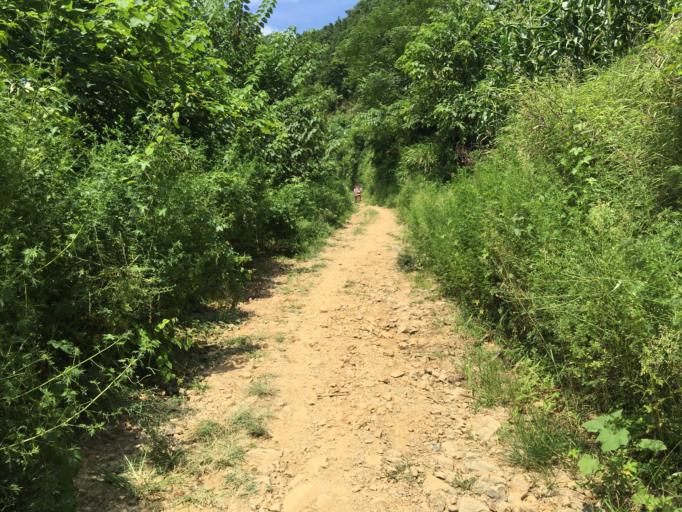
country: CN
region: Guangxi Zhuangzu Zizhiqu
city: Tongle
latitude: 24.9705
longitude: 105.9856
